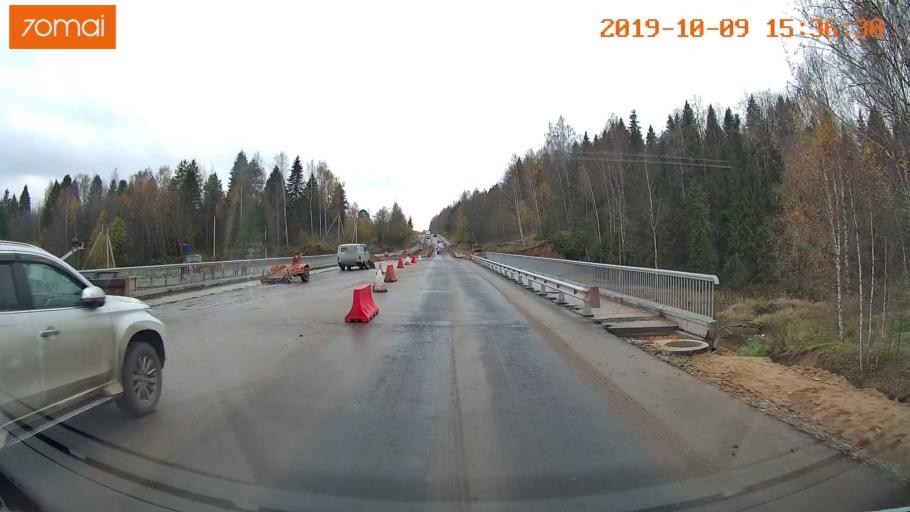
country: RU
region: Kostroma
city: Oktyabr'skiy
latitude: 57.9234
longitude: 41.2098
